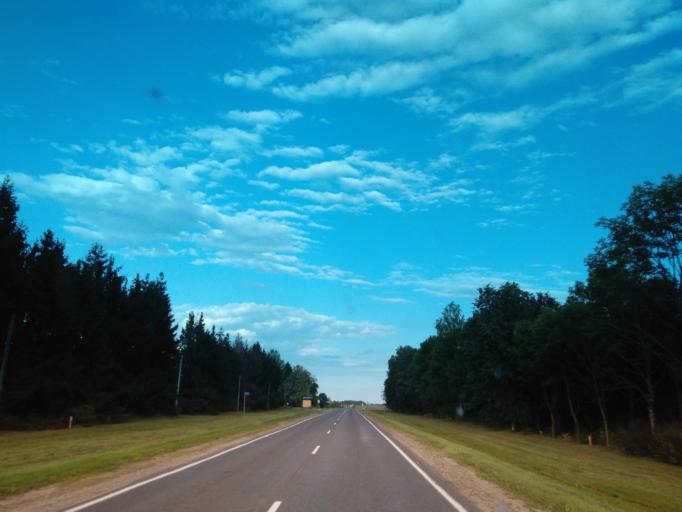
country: BY
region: Minsk
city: Uzda
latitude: 53.4378
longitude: 27.3247
